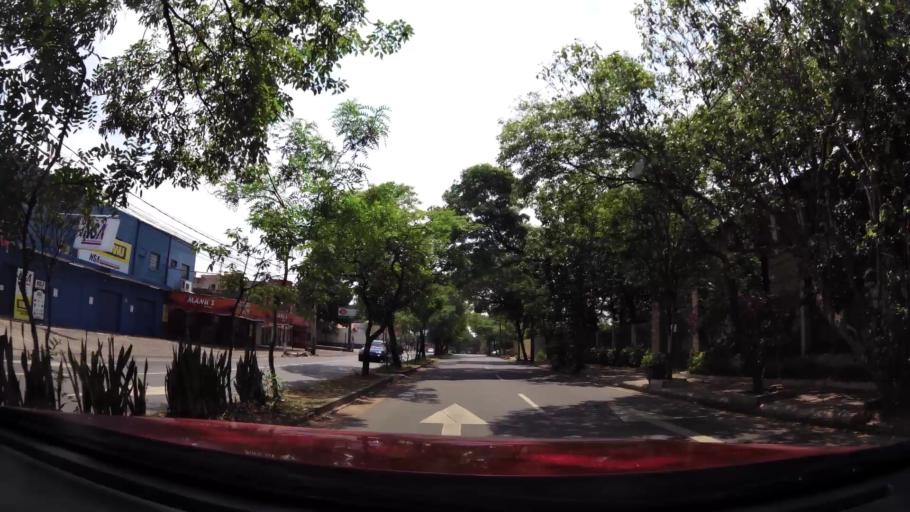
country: PY
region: Central
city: Lambare
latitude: -25.3189
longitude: -57.5922
